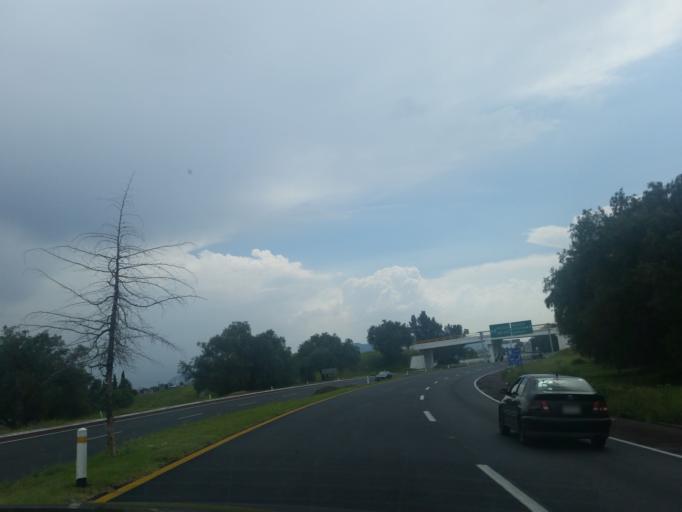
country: MX
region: Mexico
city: Acolman
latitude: 19.6186
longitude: -98.9473
